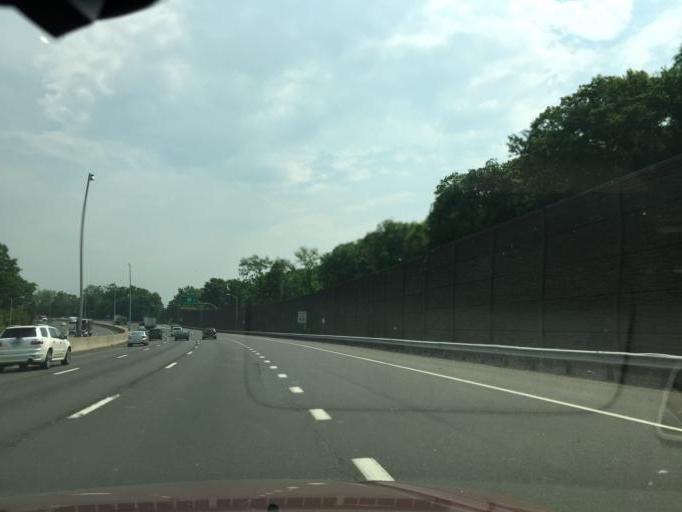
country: US
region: Connecticut
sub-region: Fairfield County
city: Darien
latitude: 41.0742
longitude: -73.4684
